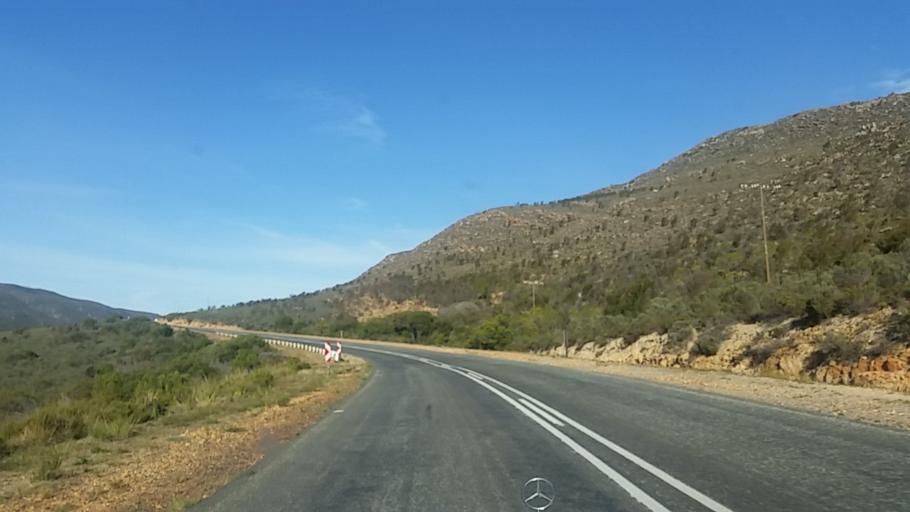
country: ZA
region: Western Cape
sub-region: Eden District Municipality
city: Knysna
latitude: -33.7514
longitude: 22.9605
